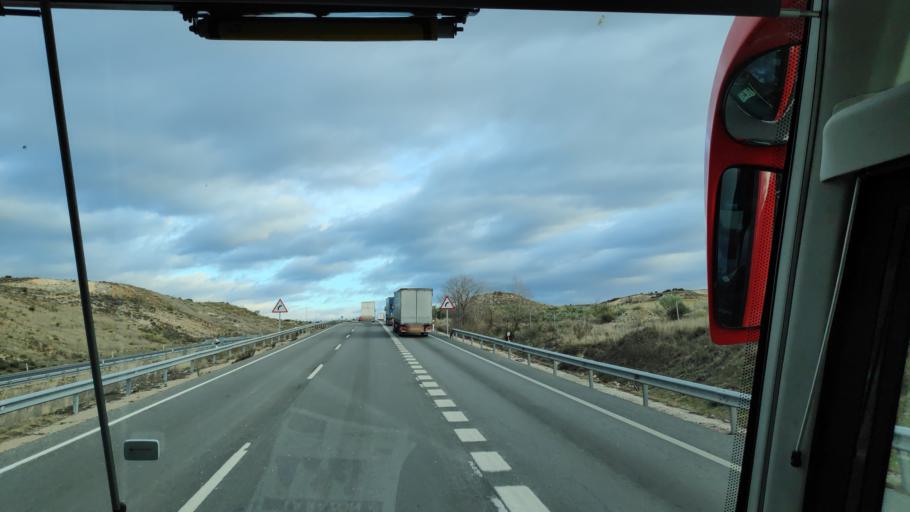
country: ES
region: Madrid
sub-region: Provincia de Madrid
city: Tielmes
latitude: 40.1985
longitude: -3.3118
